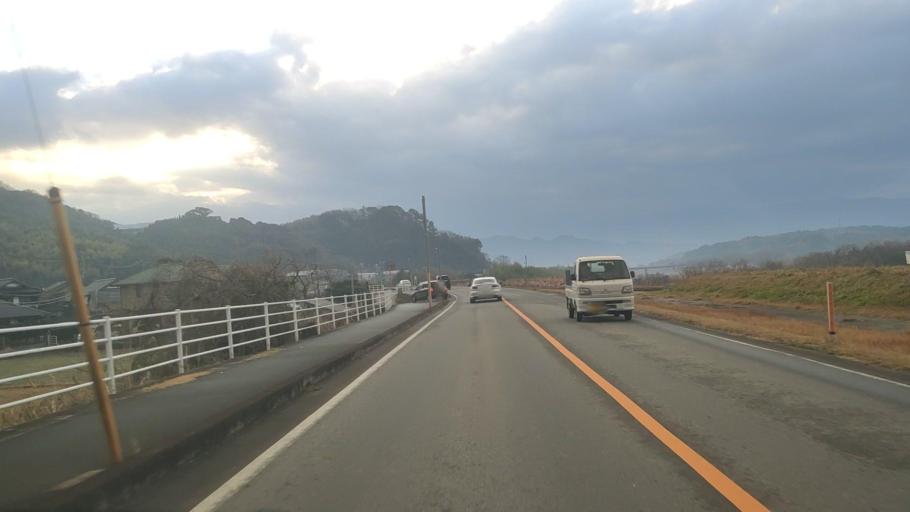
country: JP
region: Kumamoto
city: Uto
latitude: 32.7005
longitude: 130.7830
